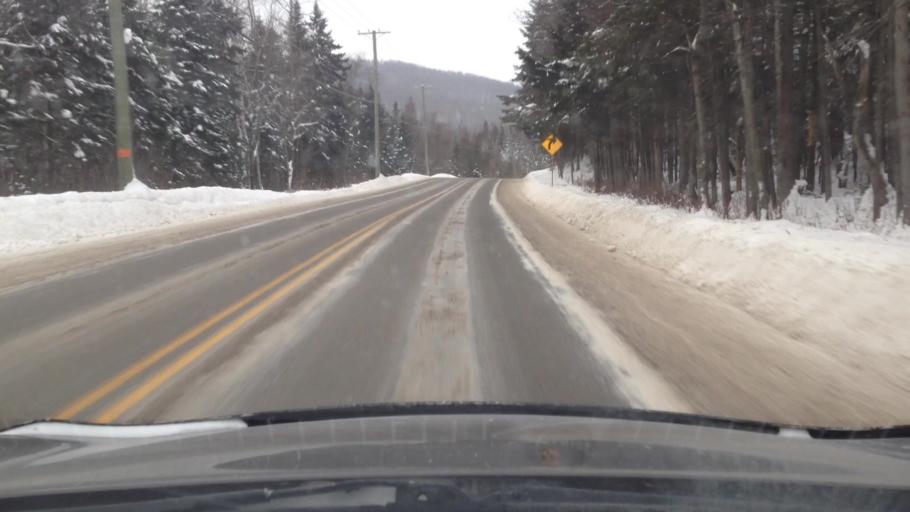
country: CA
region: Quebec
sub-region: Laurentides
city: Saint-Sauveur
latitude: 45.9073
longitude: -74.2964
